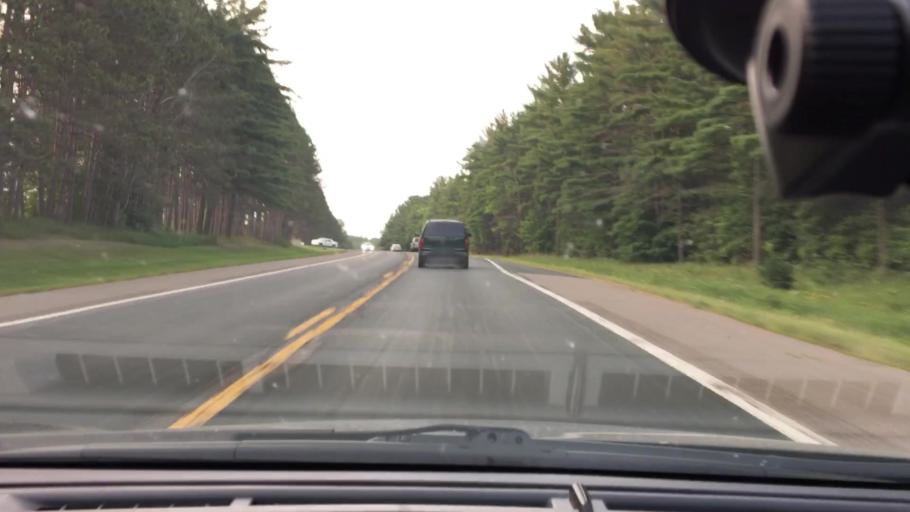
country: US
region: Minnesota
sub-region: Mille Lacs County
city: Vineland
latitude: 46.2236
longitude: -93.7918
